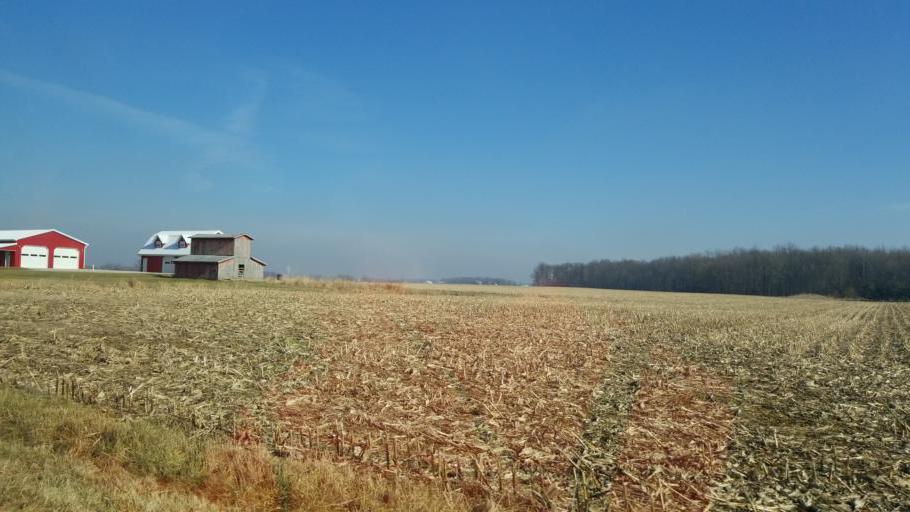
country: US
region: Ohio
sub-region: Seneca County
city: Tiffin
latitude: 40.9807
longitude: -83.0742
